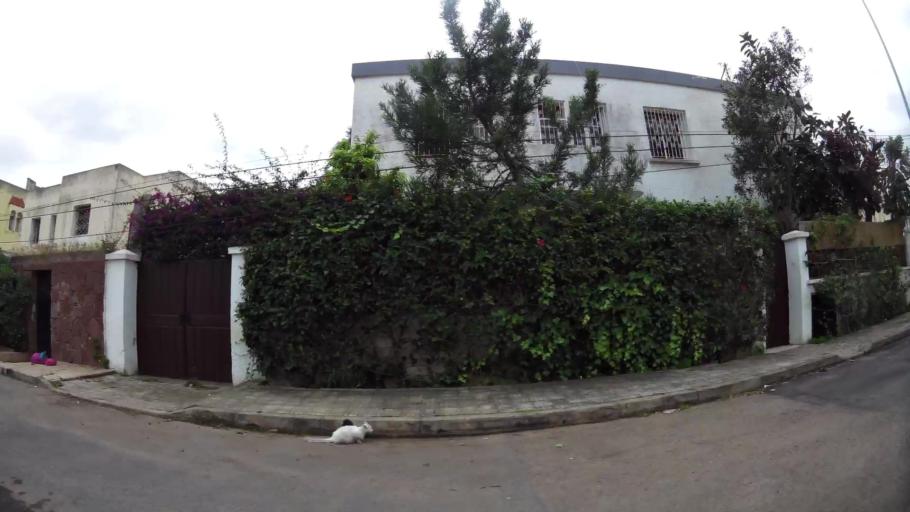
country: MA
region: Grand Casablanca
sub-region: Casablanca
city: Casablanca
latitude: 33.5516
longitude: -7.6371
